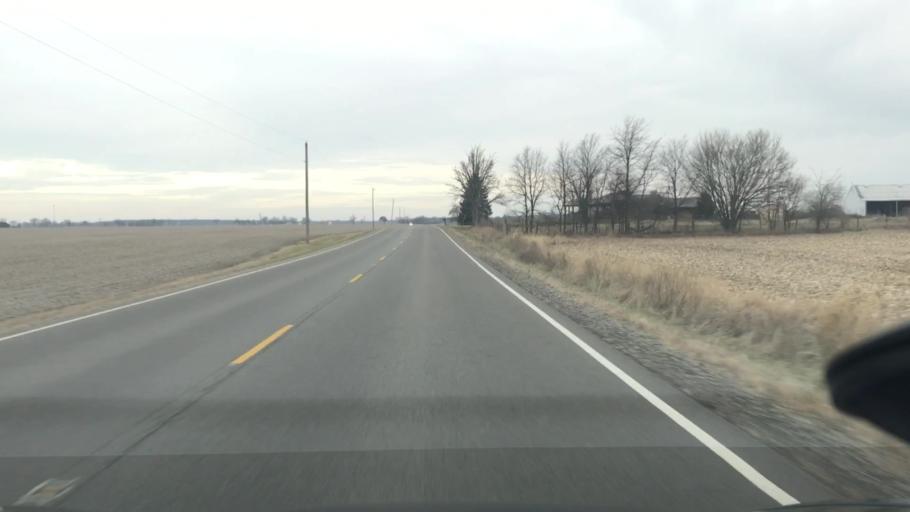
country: US
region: Ohio
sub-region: Madison County
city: Mount Sterling
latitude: 39.7899
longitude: -83.3221
